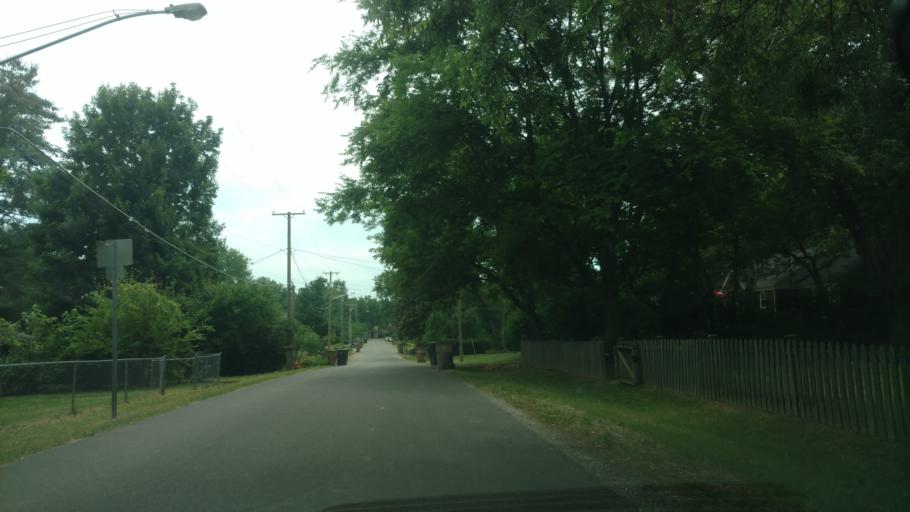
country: US
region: Tennessee
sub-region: Davidson County
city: Nashville
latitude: 36.1955
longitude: -86.7160
